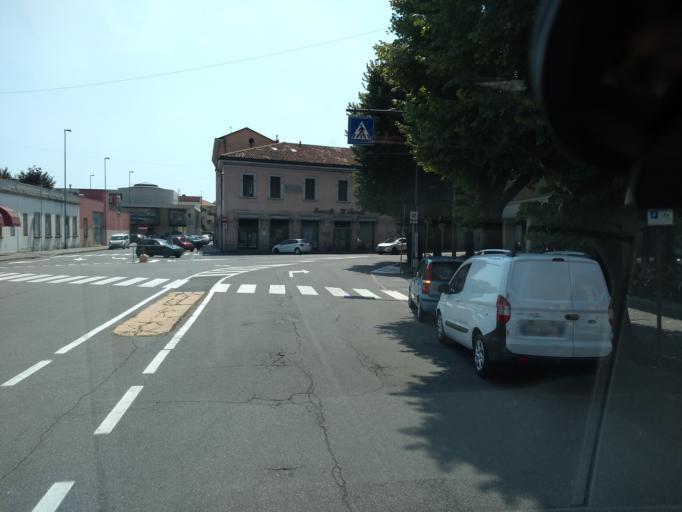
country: IT
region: Lombardy
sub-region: Provincia di Bergamo
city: Treviglio
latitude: 45.5205
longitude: 9.5953
